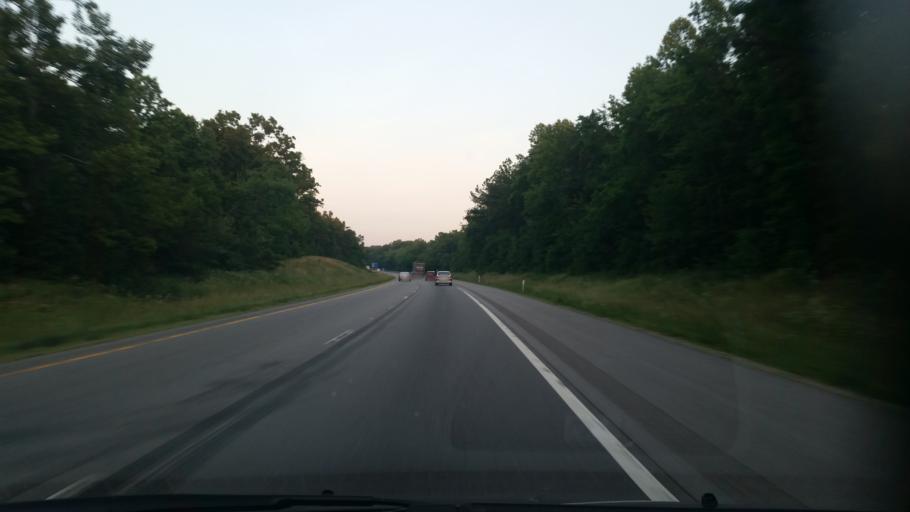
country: US
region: Tennessee
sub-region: Putnam County
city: Monterey
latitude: 36.0583
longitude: -85.1805
